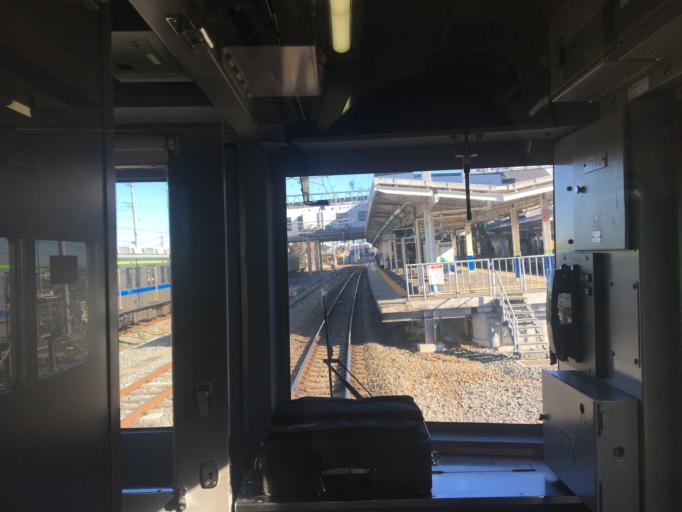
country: JP
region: Saitama
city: Iwatsuki
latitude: 35.9496
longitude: 139.6921
